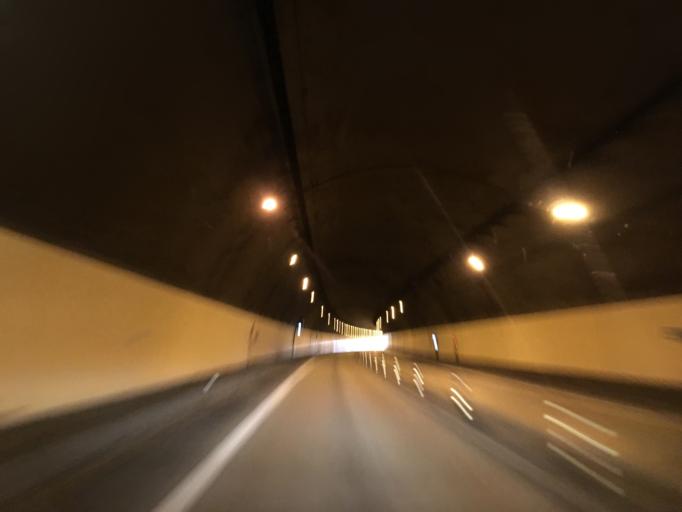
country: JP
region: Miyagi
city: Wakuya
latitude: 38.6310
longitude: 141.2813
